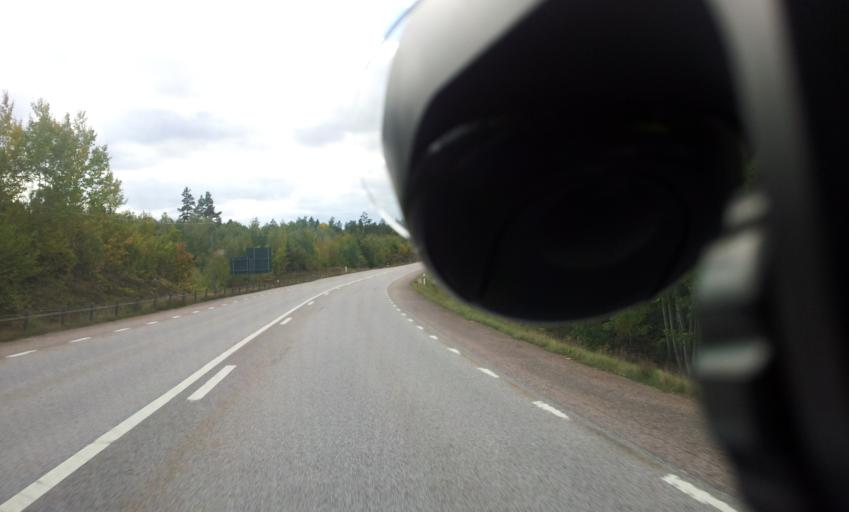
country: SE
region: Kalmar
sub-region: Oskarshamns Kommun
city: Oskarshamn
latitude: 57.4342
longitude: 16.4900
